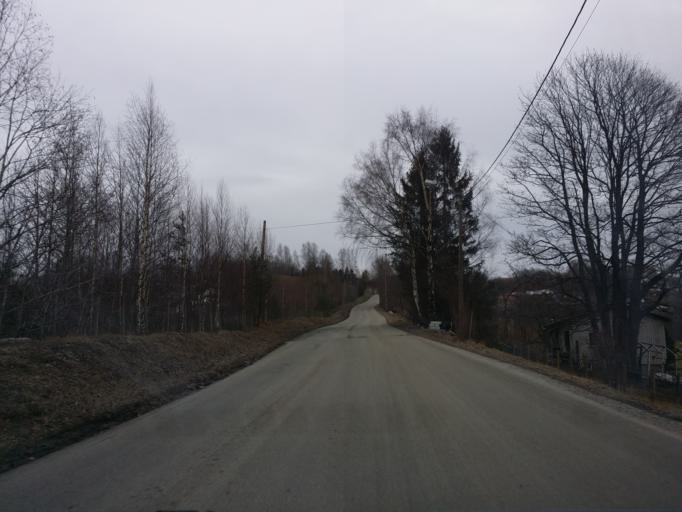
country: NO
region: Buskerud
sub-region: Lier
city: Tranby
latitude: 59.8160
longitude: 10.2422
